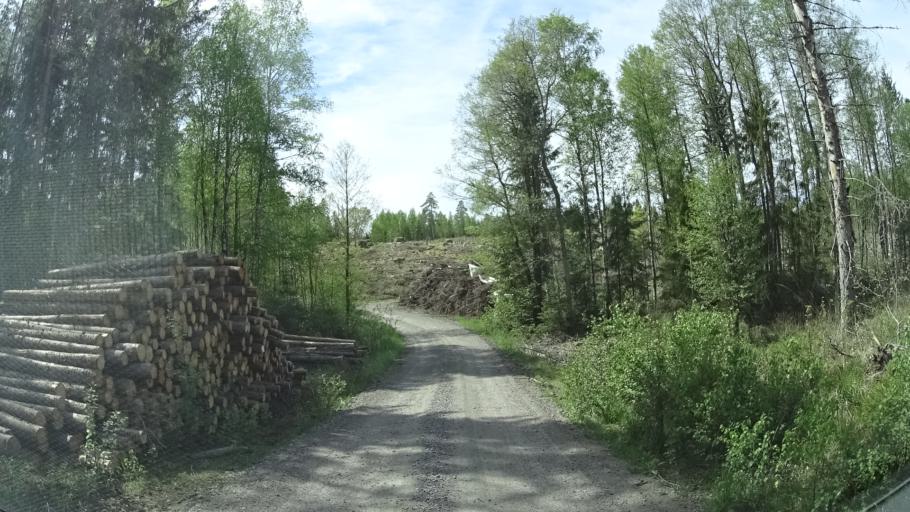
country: SE
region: OEstergoetland
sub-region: Finspangs Kommun
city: Finspang
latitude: 58.7862
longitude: 15.8470
